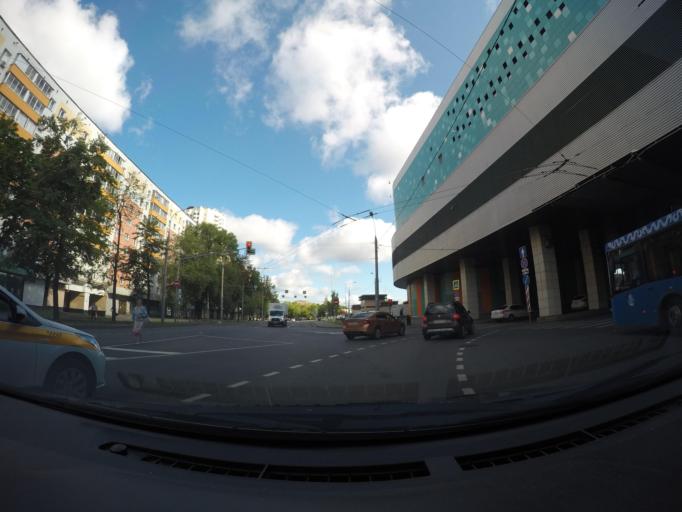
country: RU
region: Moscow
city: Khimki
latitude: 55.8630
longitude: 37.4339
